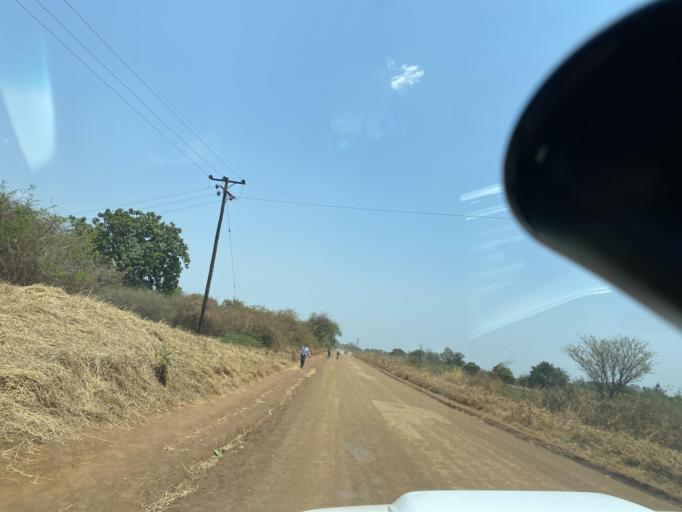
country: ZM
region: Lusaka
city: Lusaka
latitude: -15.4204
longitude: 28.1006
